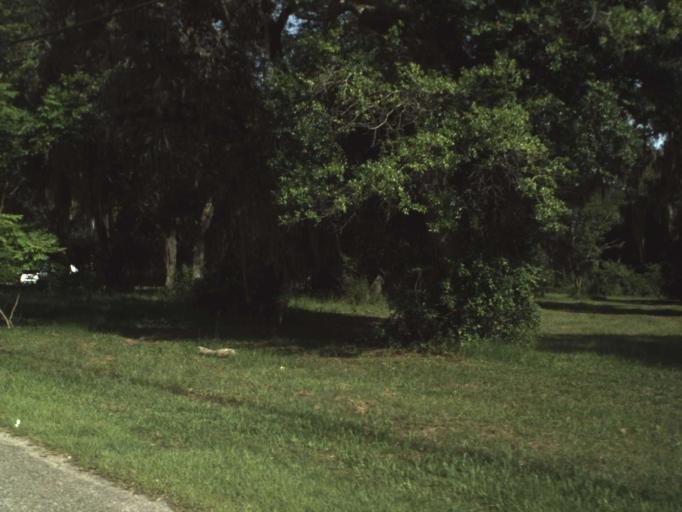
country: US
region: Florida
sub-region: Volusia County
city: DeLand
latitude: 29.0253
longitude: -81.2564
